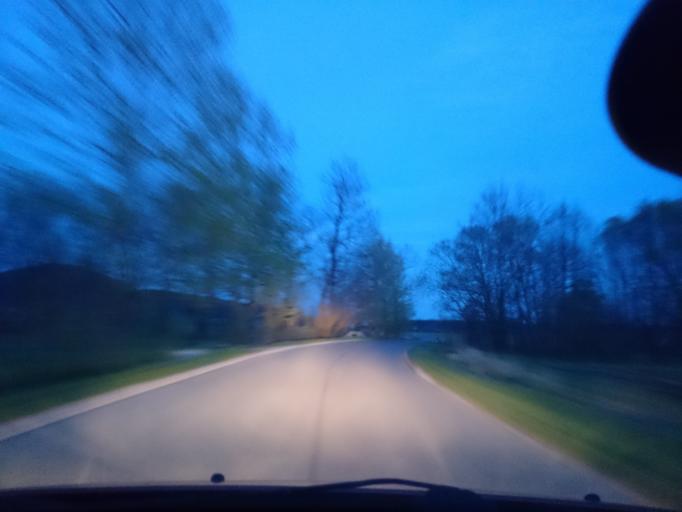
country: PL
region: Lower Silesian Voivodeship
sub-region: Powiat zabkowicki
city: Budzow
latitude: 50.5592
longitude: 16.6950
